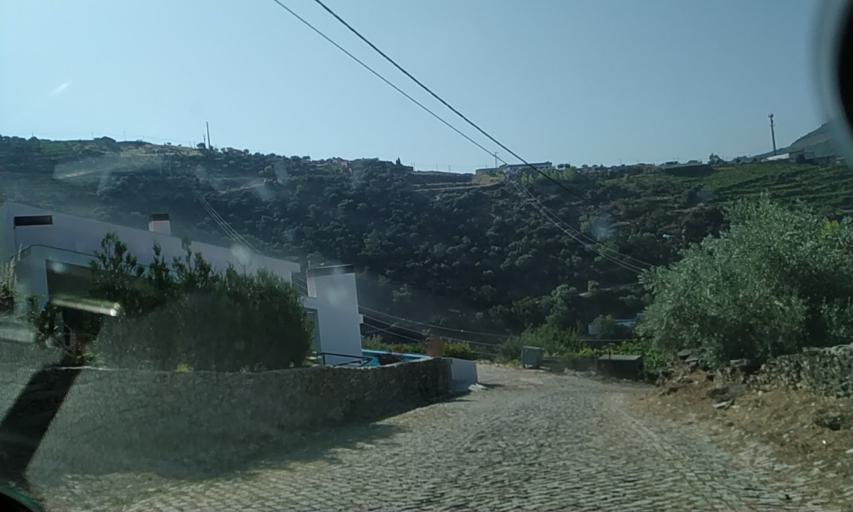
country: PT
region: Vila Real
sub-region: Sabrosa
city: Vilela
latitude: 41.1991
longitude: -7.5468
